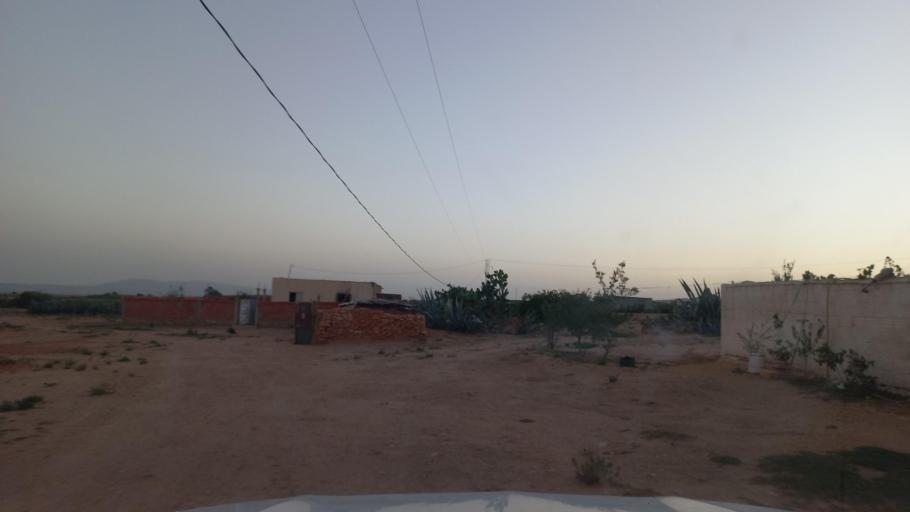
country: TN
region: Al Qasrayn
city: Sbiba
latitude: 35.3766
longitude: 9.0129
